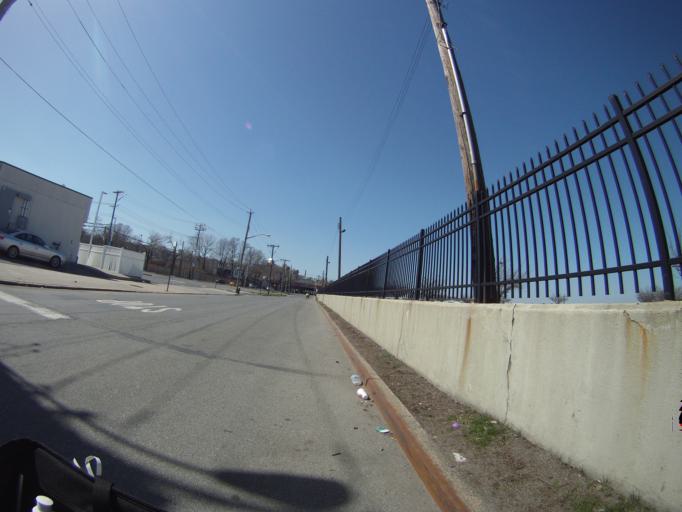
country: US
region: New Jersey
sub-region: Hudson County
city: Bayonne
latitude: 40.6197
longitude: -74.0696
